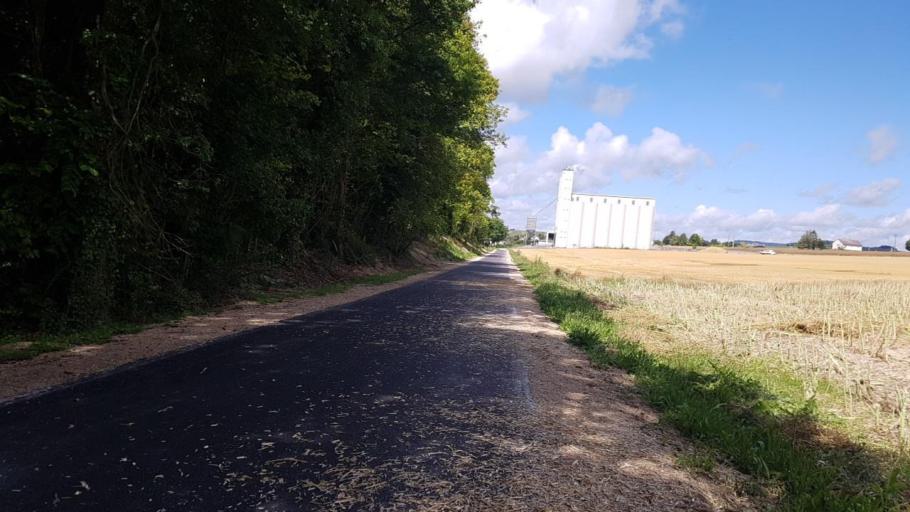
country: FR
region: Champagne-Ardenne
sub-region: Departement de la Marne
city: Tours-sur-Marne
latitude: 49.0449
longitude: 4.1030
